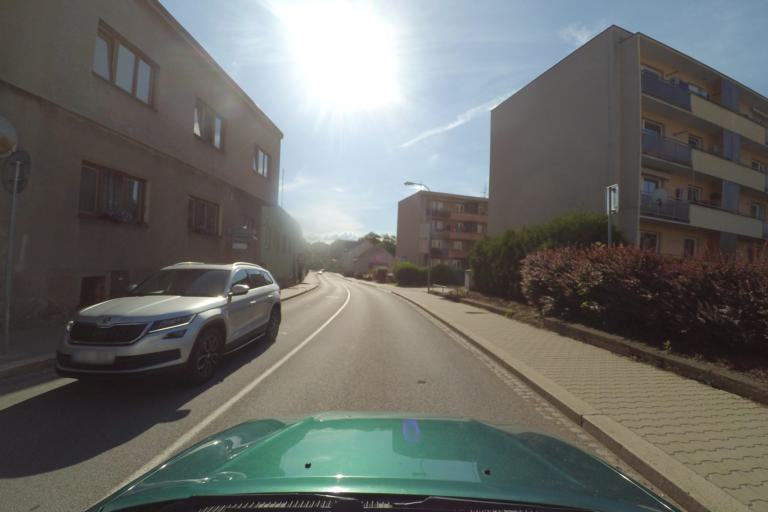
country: CZ
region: Kralovehradecky
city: Dvur Kralove nad Labem
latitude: 50.4307
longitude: 15.8178
